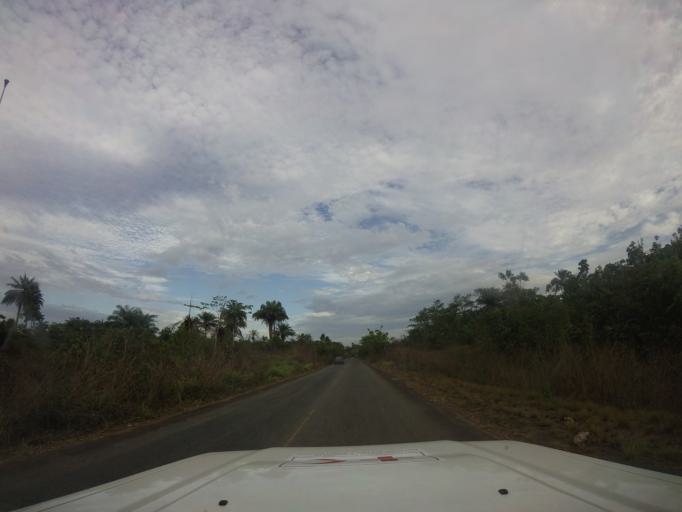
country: LR
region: Bomi
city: Tubmanburg
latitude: 6.6999
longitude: -10.9132
